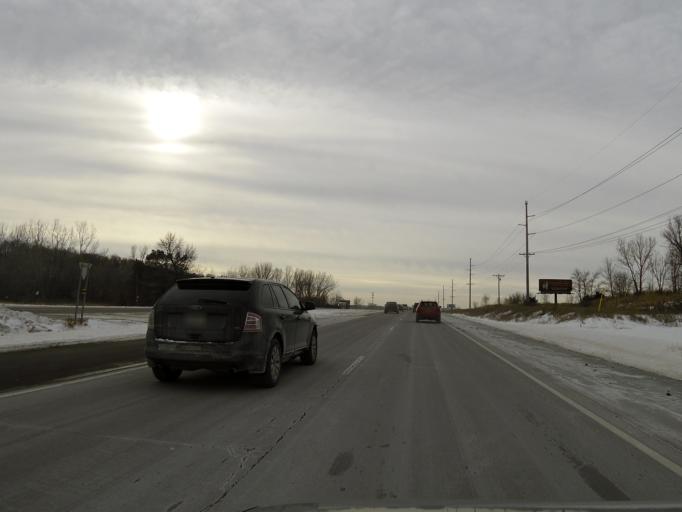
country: US
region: Minnesota
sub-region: Carver County
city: Carver
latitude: 44.7493
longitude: -93.5868
